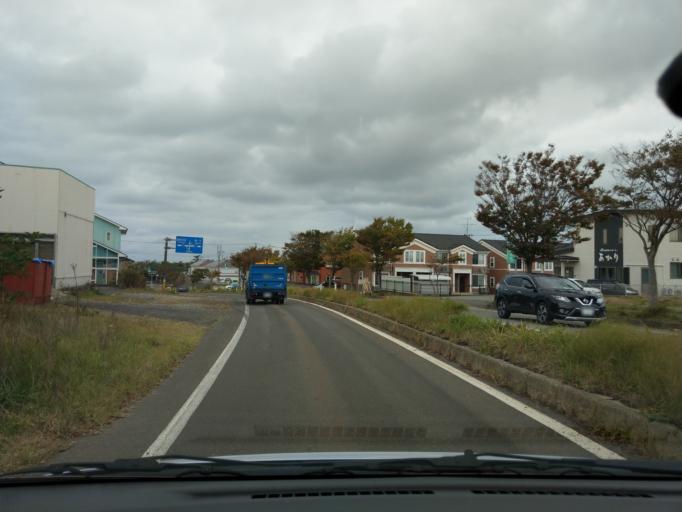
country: JP
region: Akita
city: Akita Shi
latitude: 39.6788
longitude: 140.0770
